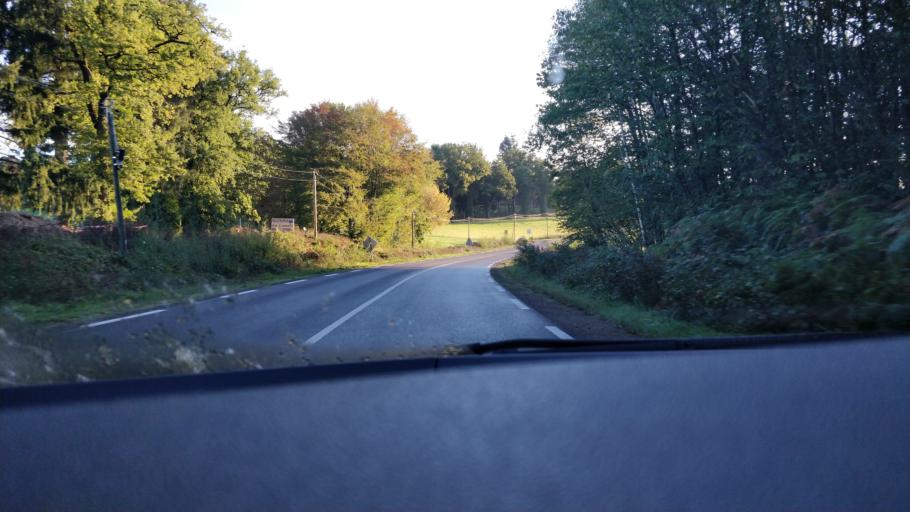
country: FR
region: Limousin
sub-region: Departement de la Haute-Vienne
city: Saint-Leonard-de-Noblat
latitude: 45.8761
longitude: 1.5427
